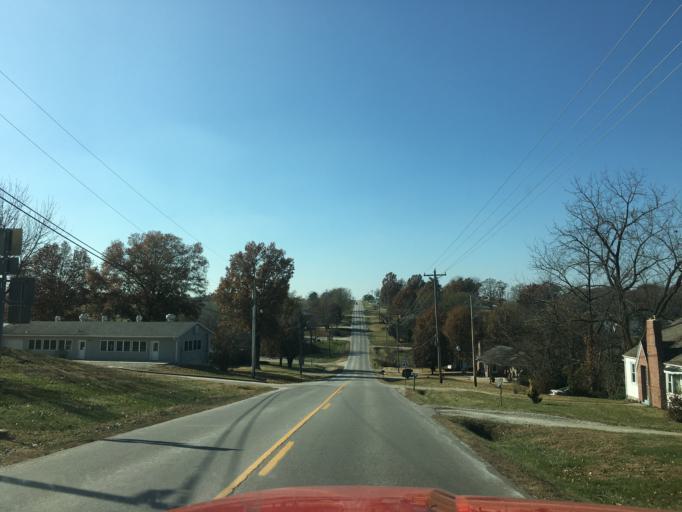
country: US
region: Missouri
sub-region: Cole County
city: Wardsville
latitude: 38.4886
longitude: -92.1769
